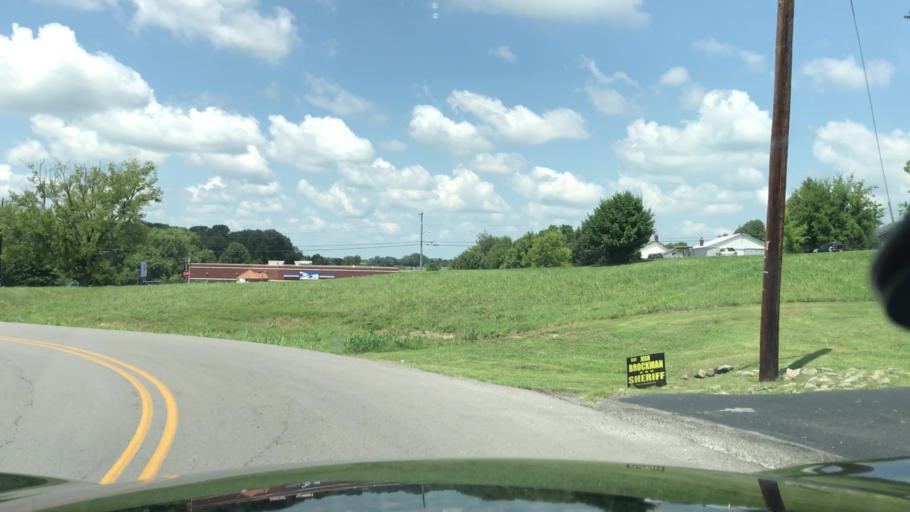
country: US
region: Kentucky
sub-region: Adair County
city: Columbia
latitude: 37.0971
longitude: -85.3130
